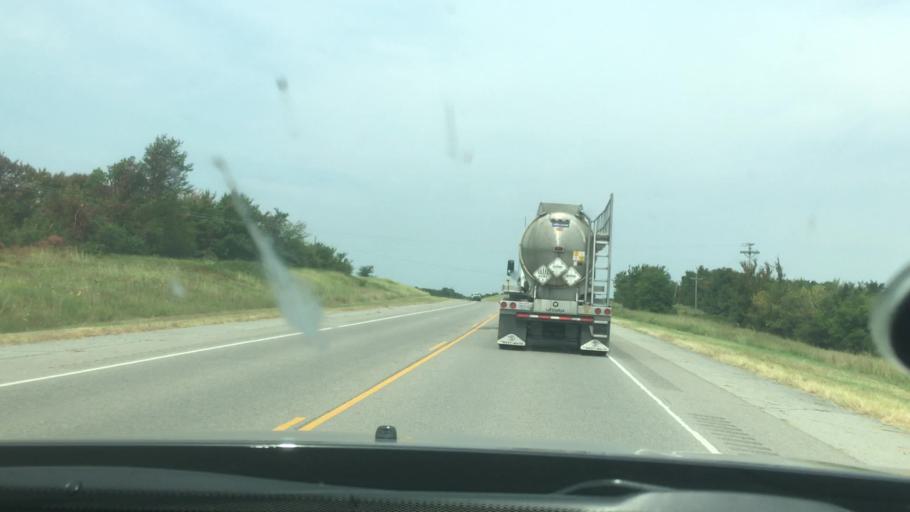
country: US
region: Oklahoma
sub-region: Pontotoc County
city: Ada
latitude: 34.6419
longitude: -96.4911
